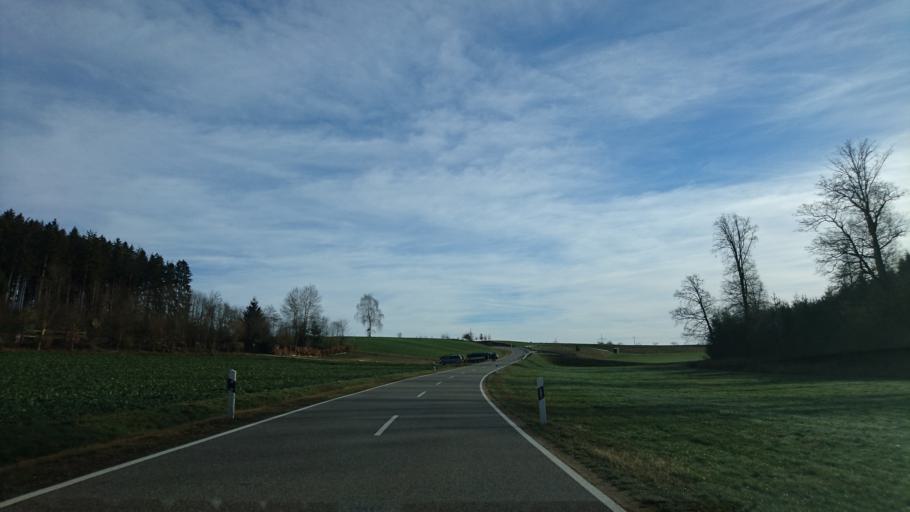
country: DE
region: Bavaria
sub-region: Swabia
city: Laugna
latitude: 48.5263
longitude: 10.7434
